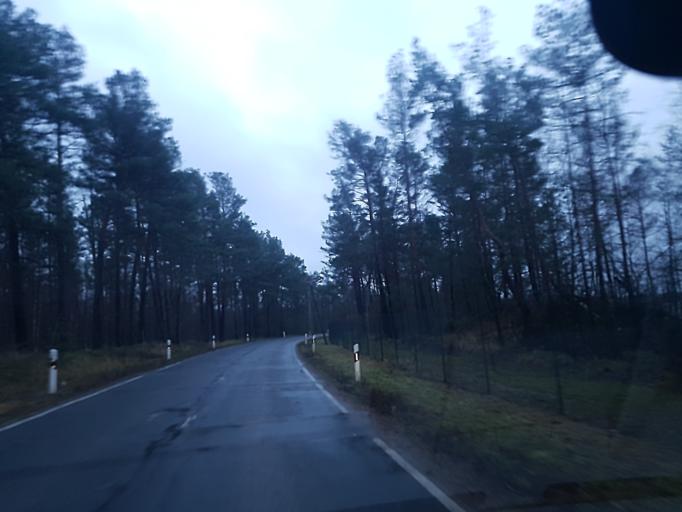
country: DE
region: Brandenburg
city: Finsterwalde
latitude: 51.6329
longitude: 13.6491
